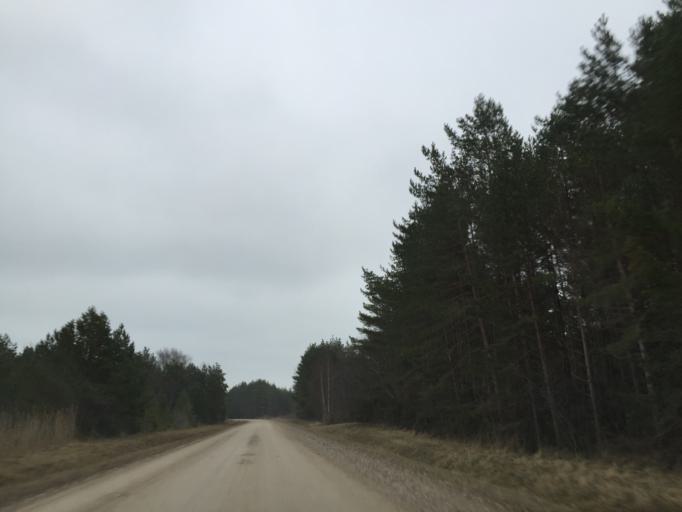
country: EE
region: Saare
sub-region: Kuressaare linn
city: Kuressaare
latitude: 58.1384
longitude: 22.2385
